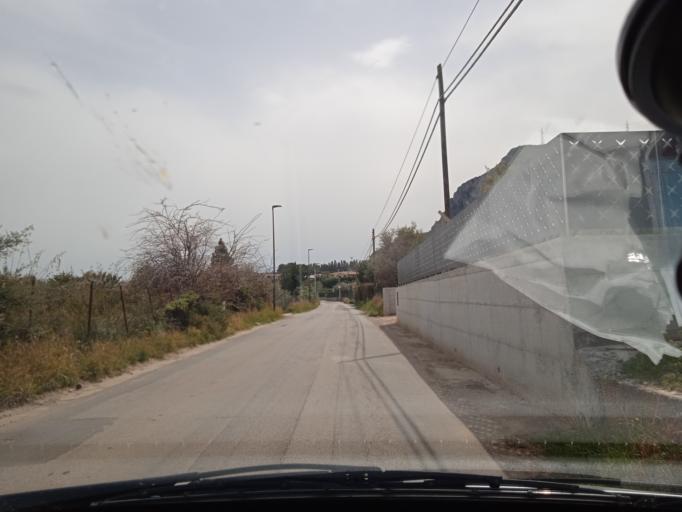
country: IT
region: Sicily
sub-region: Palermo
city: Torre Colonna-Sperone
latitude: 38.0274
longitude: 13.5736
